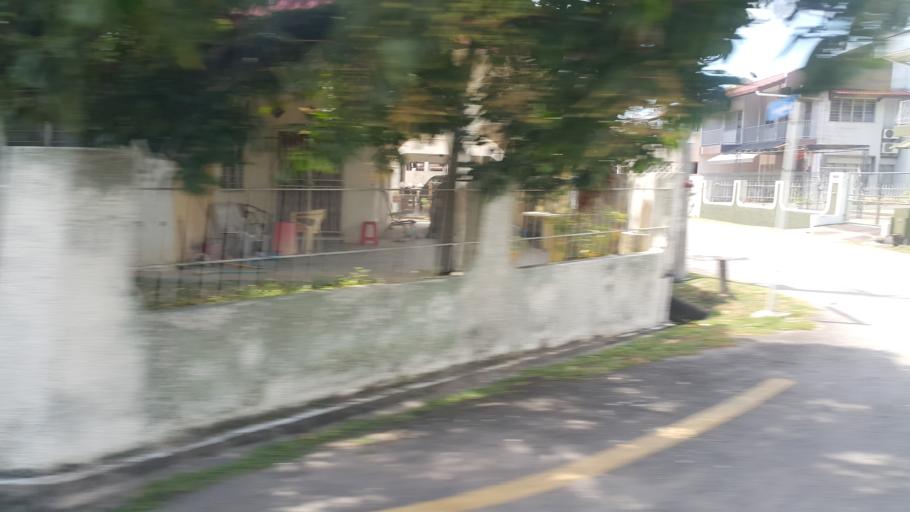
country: MY
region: Melaka
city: Kampung Bukit Baharu
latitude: 2.1870
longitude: 102.2720
